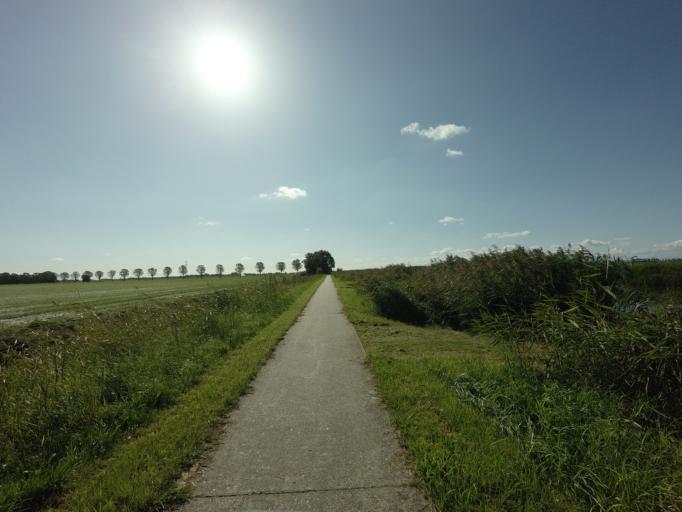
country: NL
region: Friesland
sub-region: Gemeente Boarnsterhim
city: Reduzum
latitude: 53.1223
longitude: 5.7557
